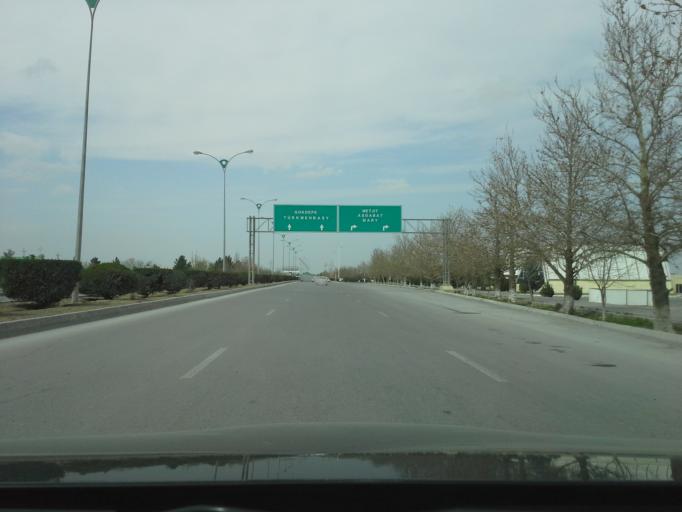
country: TM
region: Ahal
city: Abadan
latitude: 38.0491
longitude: 58.1861
